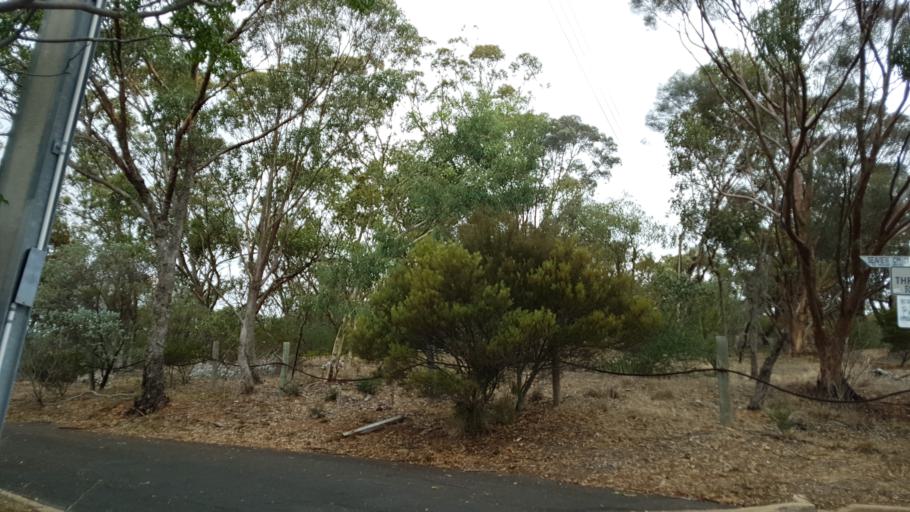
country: AU
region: South Australia
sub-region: Mitcham
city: Clapham
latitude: -35.0056
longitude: 138.5983
